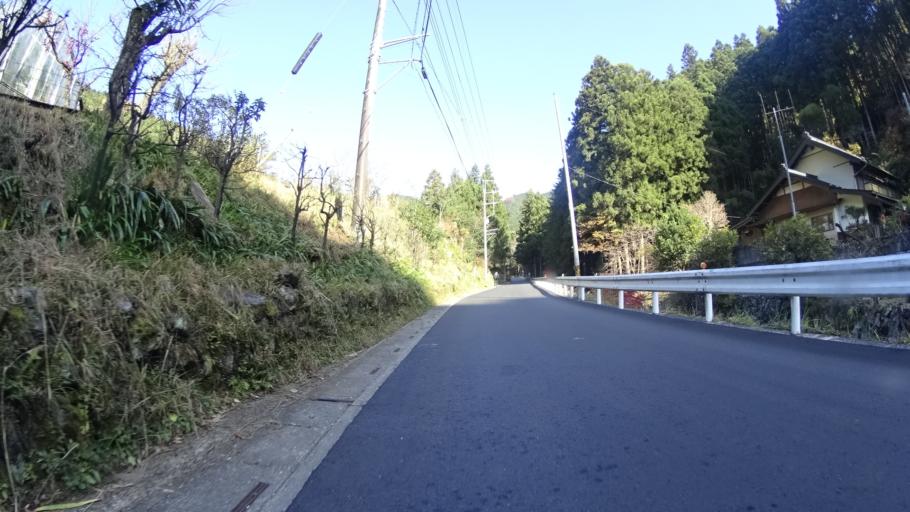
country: JP
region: Saitama
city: Chichibu
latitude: 35.9187
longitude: 139.1505
